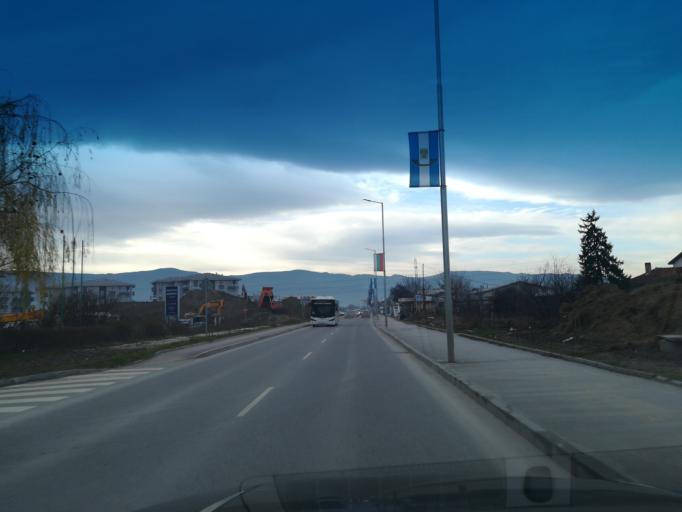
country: BG
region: Plovdiv
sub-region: Obshtina Plovdiv
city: Plovdiv
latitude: 42.1141
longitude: 24.7111
